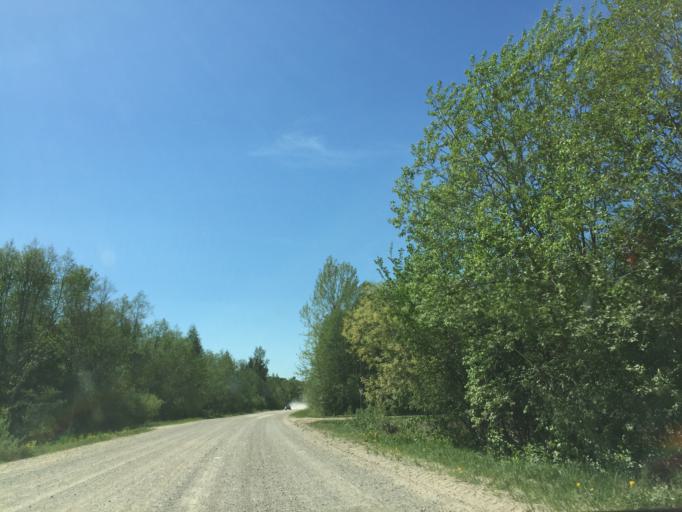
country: LV
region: Kegums
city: Kegums
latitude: 56.8699
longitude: 24.7750
